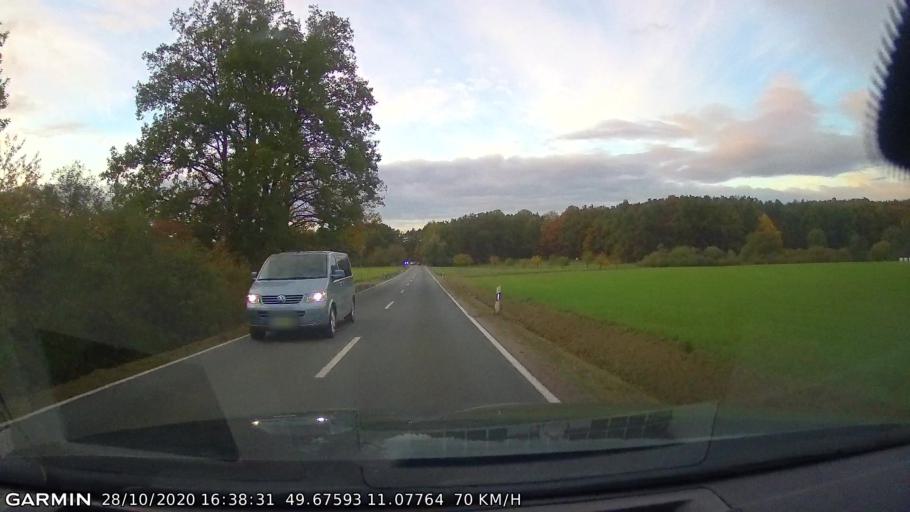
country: DE
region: Bavaria
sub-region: Upper Franconia
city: Poxdorf
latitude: 49.6760
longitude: 11.0776
